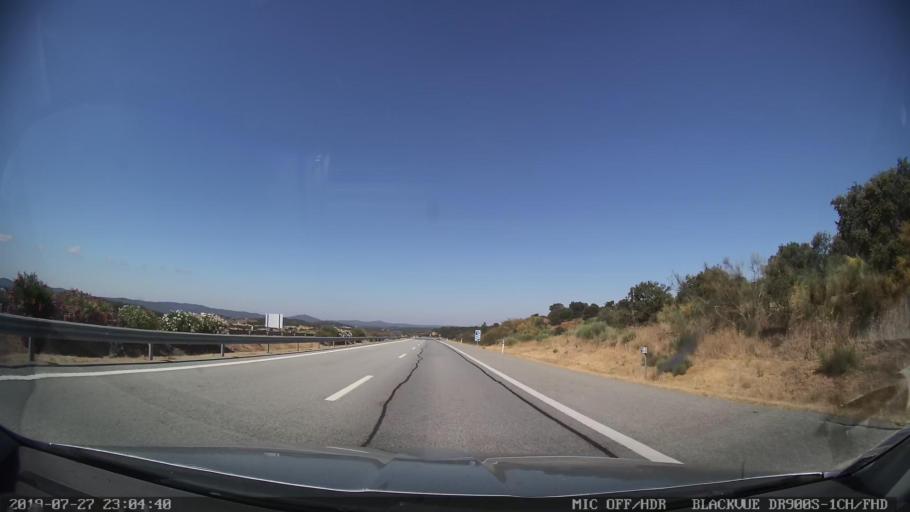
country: PT
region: Evora
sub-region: Estremoz
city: Estremoz
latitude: 38.8231
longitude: -7.5917
